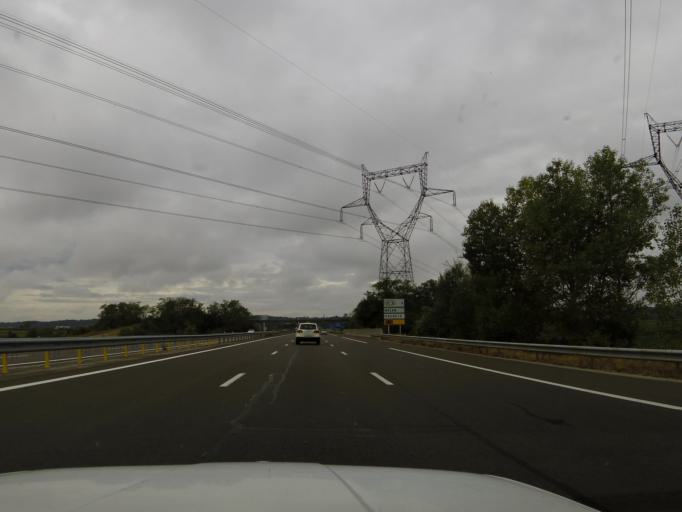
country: FR
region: Rhone-Alpes
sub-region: Departement de l'Ain
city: Beligneux
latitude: 45.8621
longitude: 5.1625
